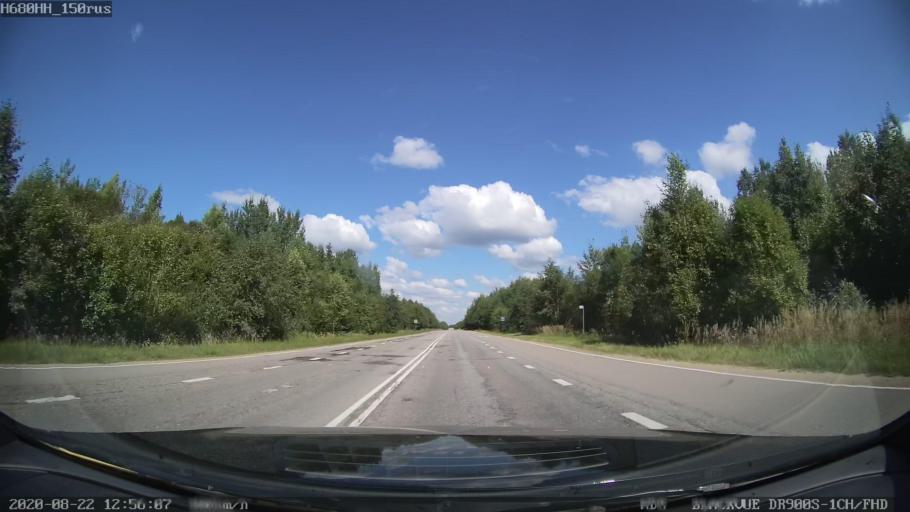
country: RU
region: Tverskaya
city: Rameshki
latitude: 57.5517
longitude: 36.3127
